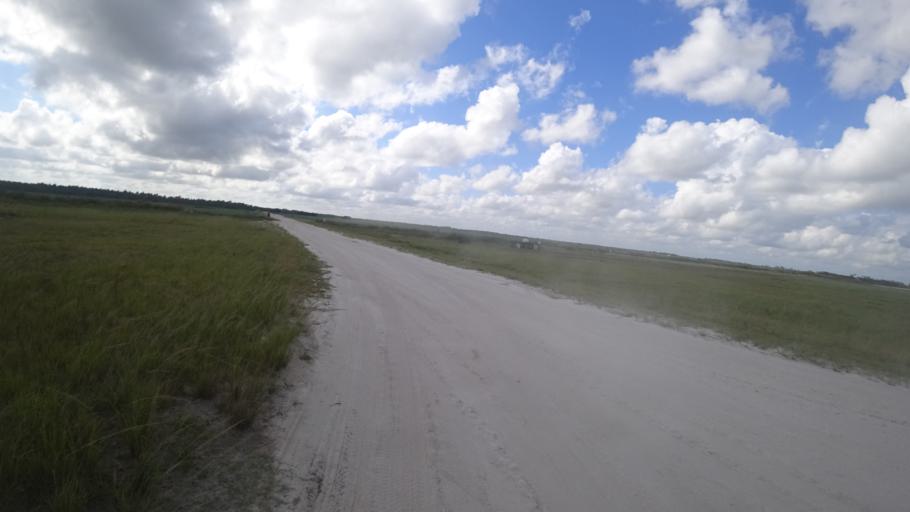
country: US
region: Florida
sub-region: Sarasota County
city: Lake Sarasota
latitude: 27.4131
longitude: -82.2000
